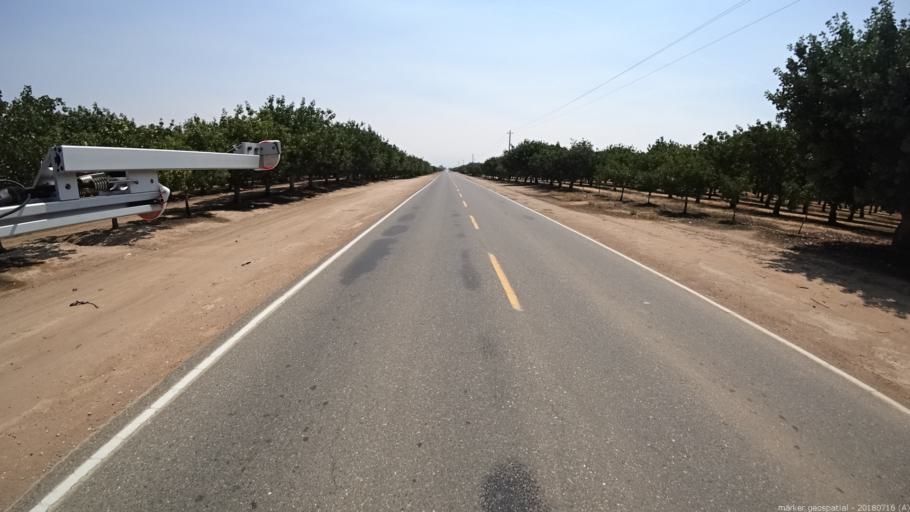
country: US
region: California
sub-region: Madera County
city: Madera Acres
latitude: 37.0543
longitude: -120.0472
